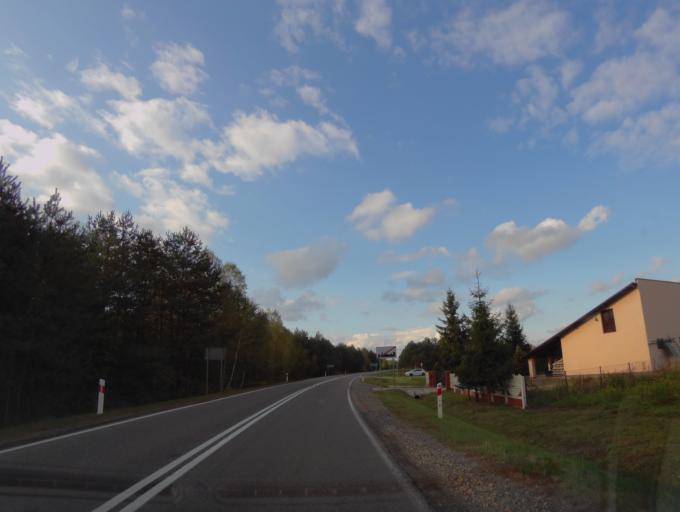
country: PL
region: Subcarpathian Voivodeship
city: Nowa Sarzyna
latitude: 50.3351
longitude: 22.3326
